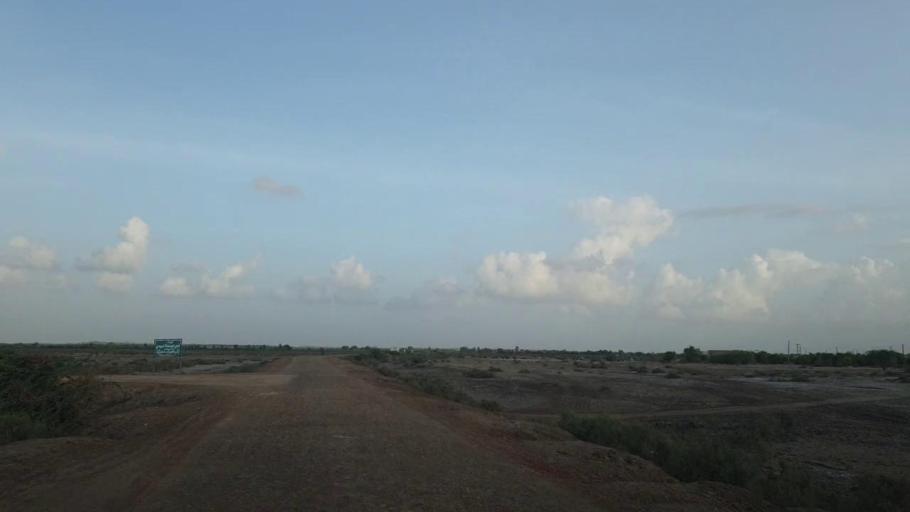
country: PK
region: Sindh
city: Kadhan
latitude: 24.5553
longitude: 69.1226
